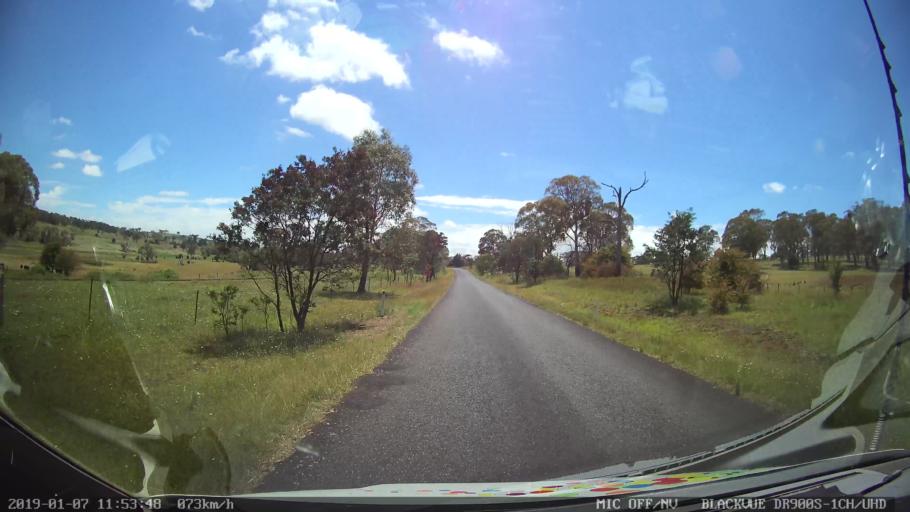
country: AU
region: New South Wales
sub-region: Guyra
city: Guyra
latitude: -30.3021
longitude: 151.6612
